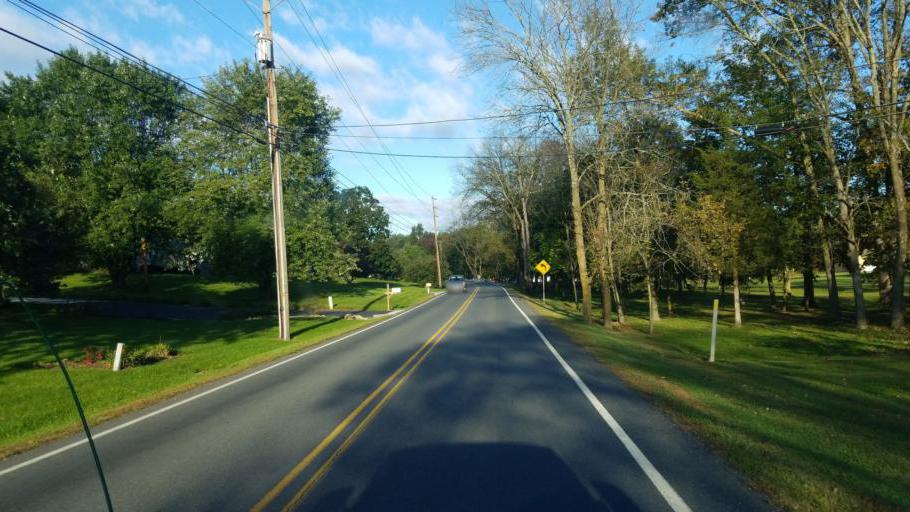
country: US
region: Pennsylvania
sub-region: Adams County
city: Gettysburg
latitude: 39.8594
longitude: -77.2337
